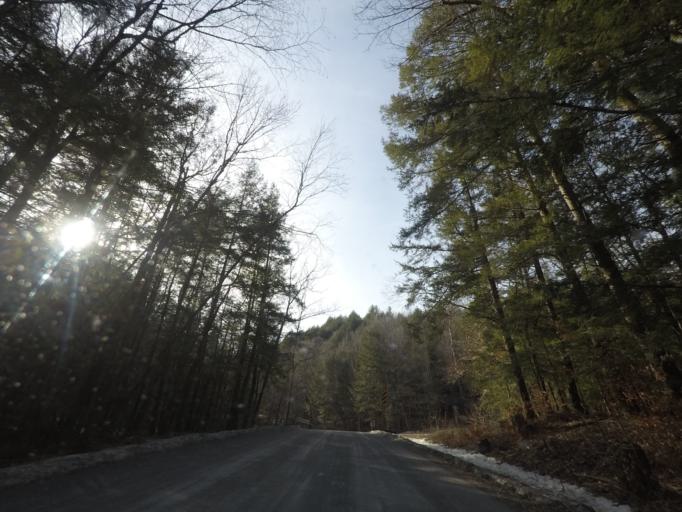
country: US
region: New York
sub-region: Rensselaer County
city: Hoosick Falls
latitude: 42.7662
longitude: -73.3522
